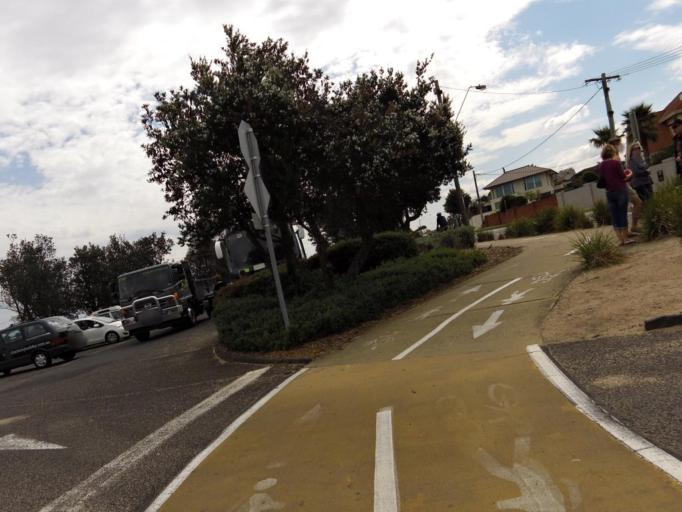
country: AU
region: Victoria
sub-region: Bayside
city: North Brighton
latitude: -37.9178
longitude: 144.9873
